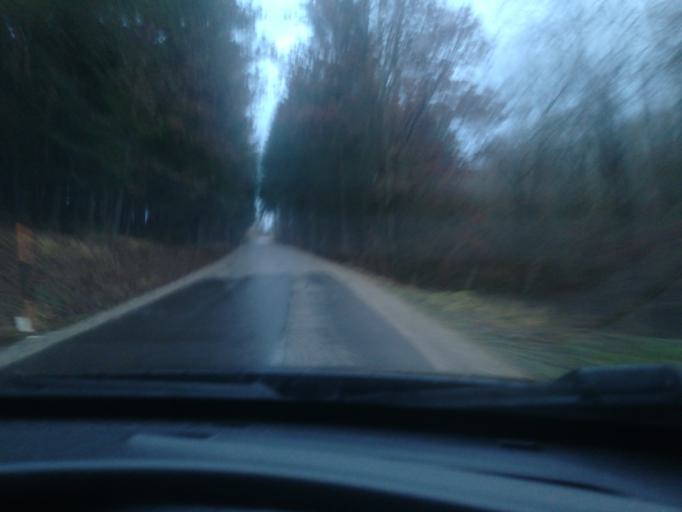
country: AT
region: Upper Austria
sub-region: Politischer Bezirk Perg
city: Perg
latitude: 48.3053
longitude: 14.6262
